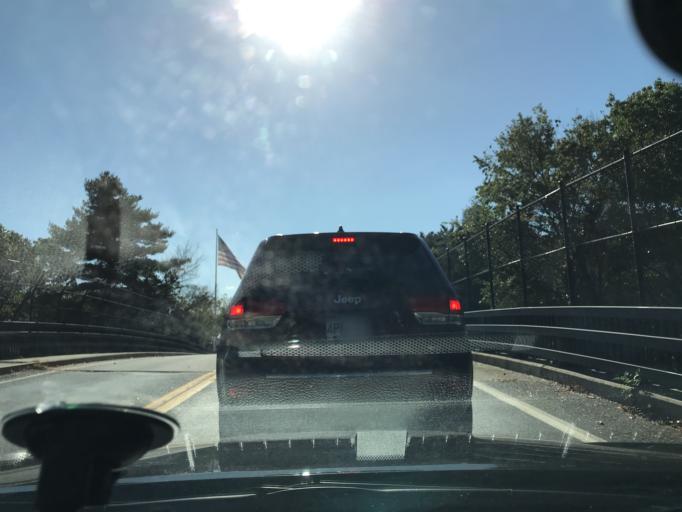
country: US
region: Massachusetts
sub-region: Norfolk County
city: Wellesley
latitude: 42.2965
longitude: -71.2996
